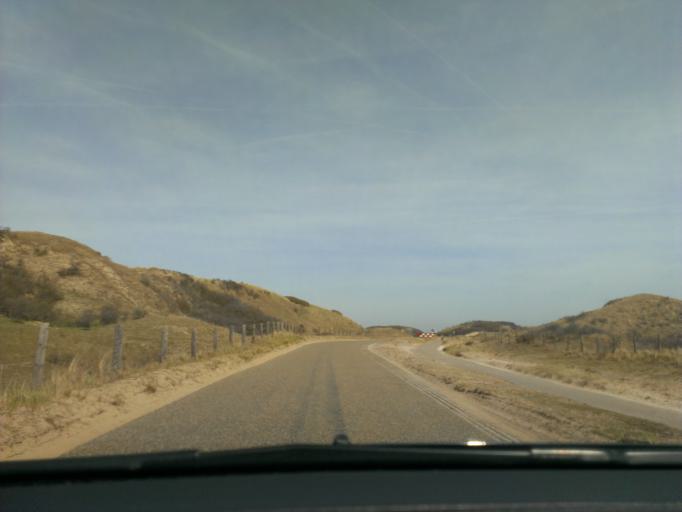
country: NL
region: North Holland
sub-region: Gemeente Zandvoort
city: Zandvoort
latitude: 52.4136
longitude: 4.5524
